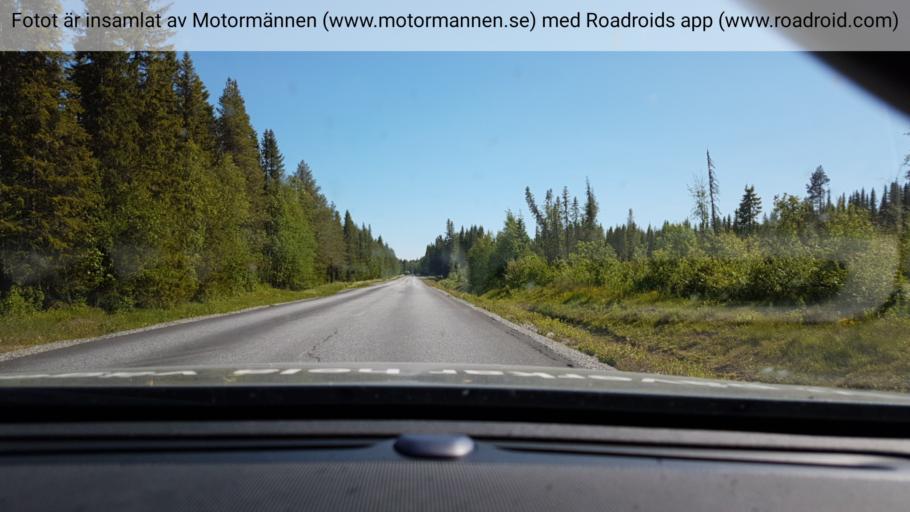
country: SE
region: Vaesterbotten
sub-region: Vilhelmina Kommun
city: Sjoberg
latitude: 64.7271
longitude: 16.2260
